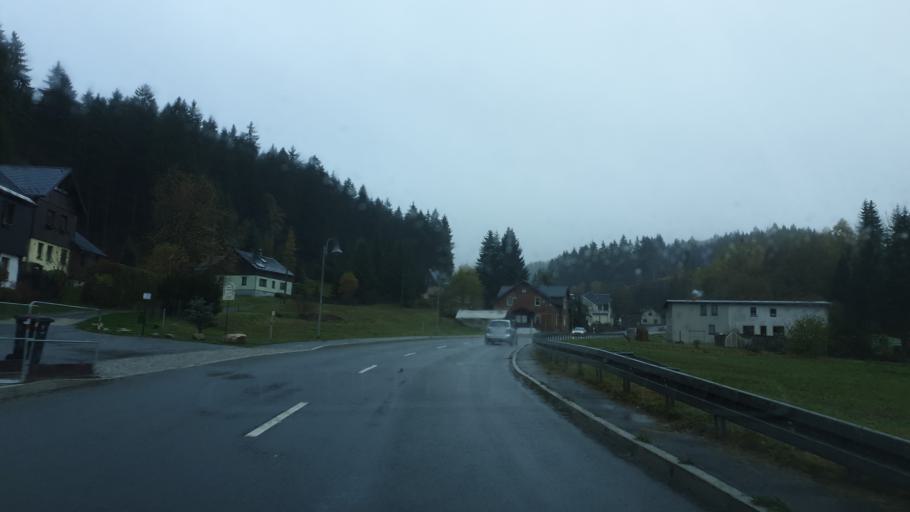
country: DE
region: Saxony
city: Tannenbergsthal
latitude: 50.4309
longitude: 12.4700
